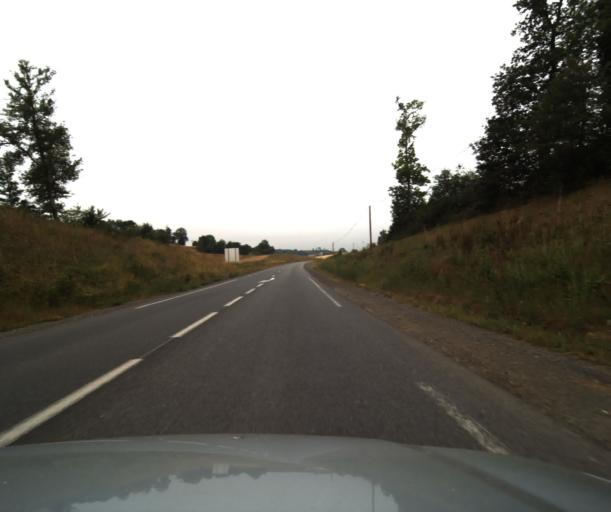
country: FR
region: Midi-Pyrenees
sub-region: Departement du Gers
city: Aubiet
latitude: 43.6482
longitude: 0.7222
